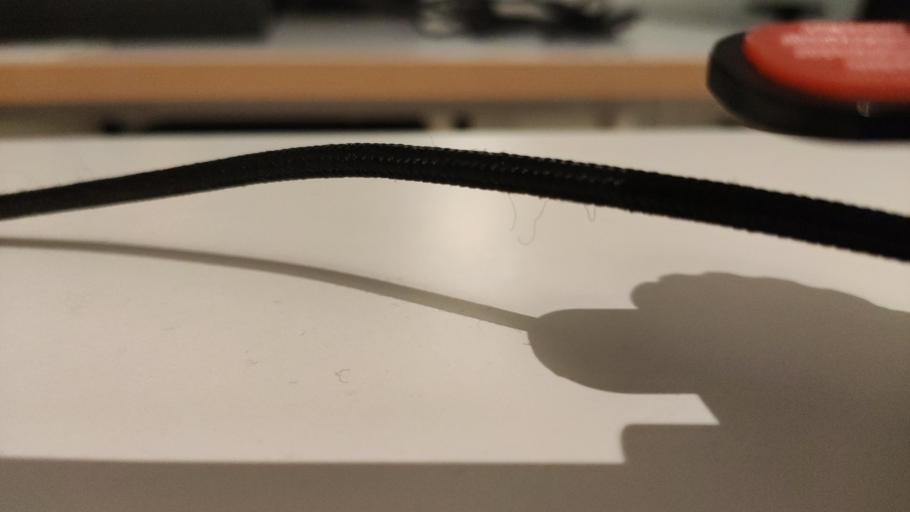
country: RU
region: Moskovskaya
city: Dmitrov
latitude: 56.3540
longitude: 37.5235
